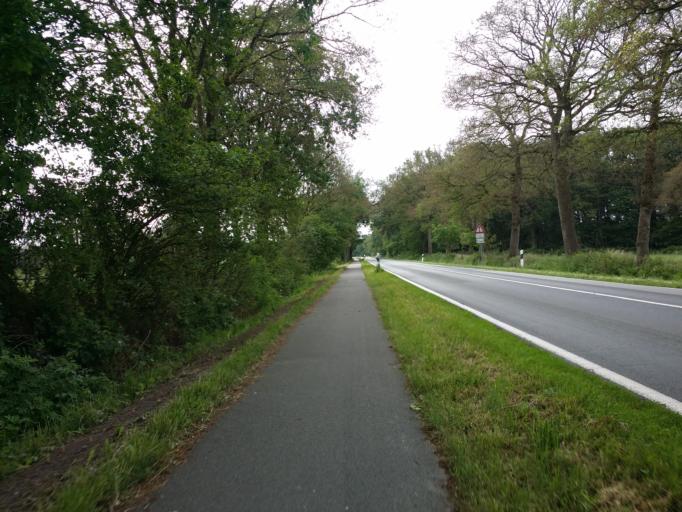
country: DE
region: Lower Saxony
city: Wittmund
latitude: 53.5167
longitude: 7.7928
